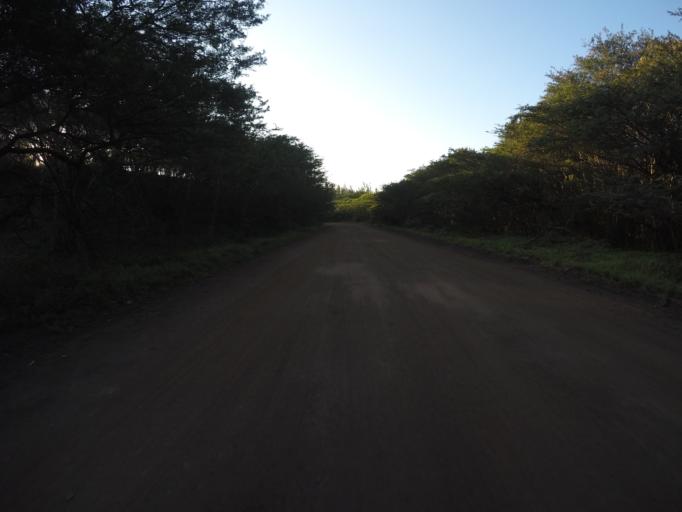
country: ZA
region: KwaZulu-Natal
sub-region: uThungulu District Municipality
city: KwaMbonambi
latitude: -28.6923
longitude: 32.2095
